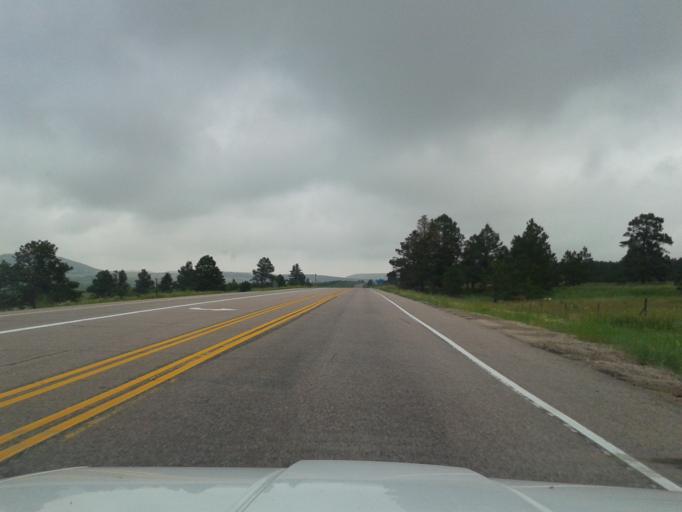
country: US
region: Colorado
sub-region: El Paso County
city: Woodmoor
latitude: 39.1299
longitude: -104.7665
